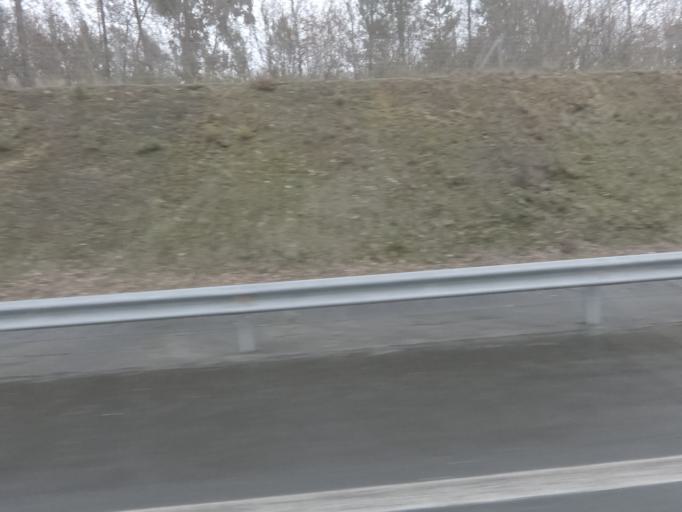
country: ES
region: Galicia
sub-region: Provincia da Coruna
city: Santiago de Compostela
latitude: 42.8273
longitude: -8.5216
